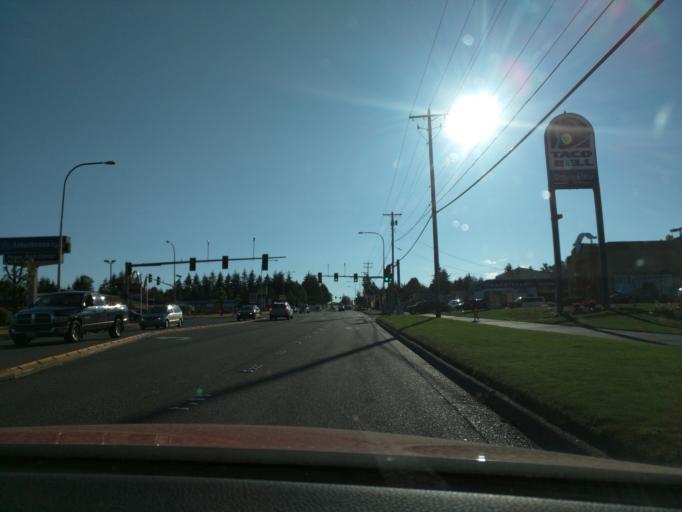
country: US
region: Washington
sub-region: Snohomish County
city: Martha Lake
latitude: 47.8820
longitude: -122.2402
